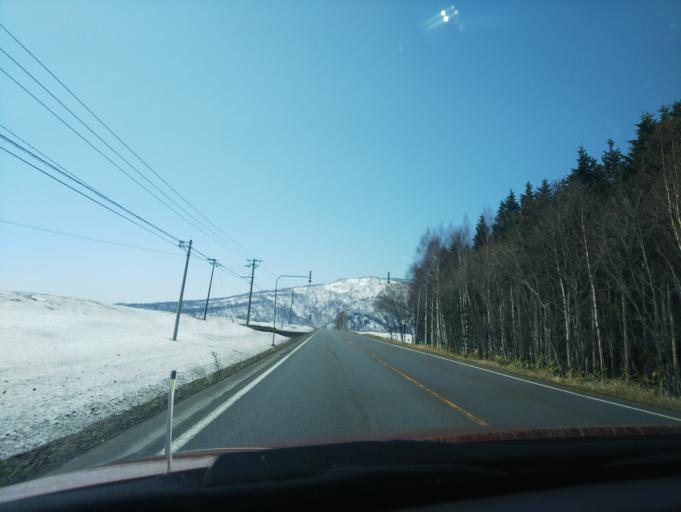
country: JP
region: Hokkaido
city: Nayoro
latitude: 44.6558
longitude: 142.2701
